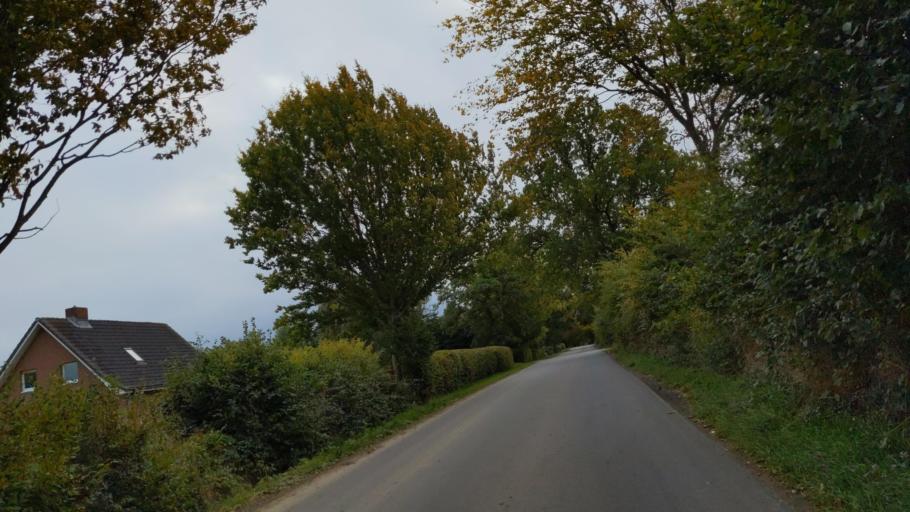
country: DE
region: Schleswig-Holstein
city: Sierksdorf
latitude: 54.0806
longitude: 10.7440
